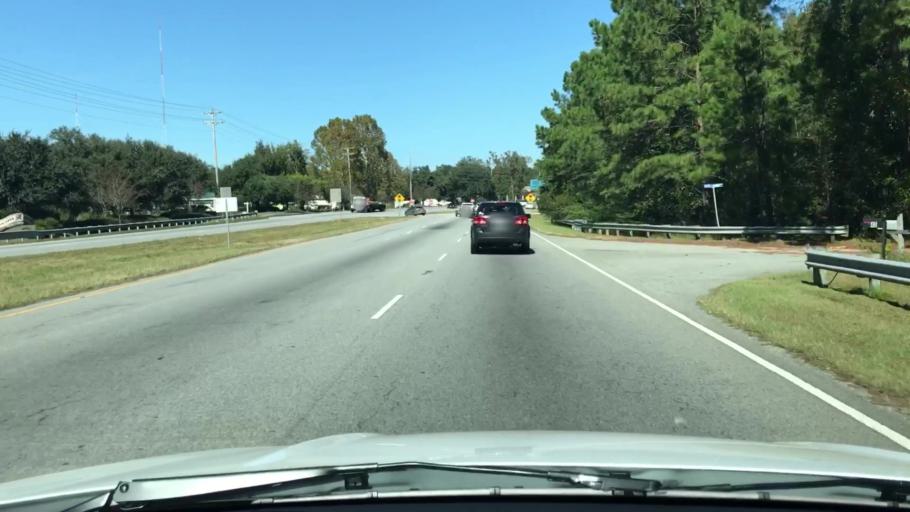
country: US
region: South Carolina
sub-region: Beaufort County
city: Bluffton
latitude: 32.3190
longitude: -80.9342
